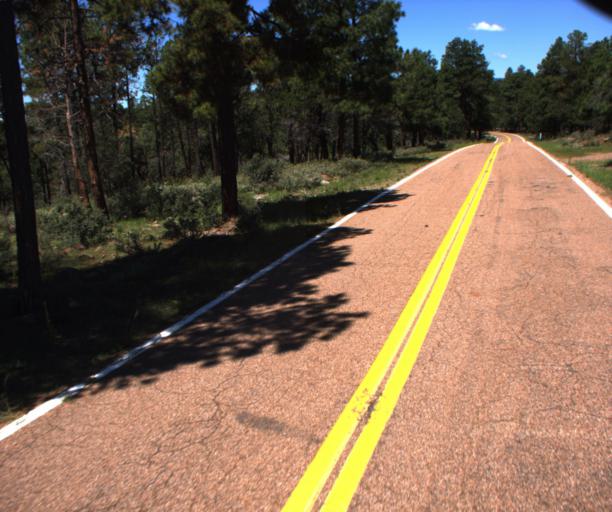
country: US
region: Arizona
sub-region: Greenlee County
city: Morenci
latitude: 33.5155
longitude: -109.3139
